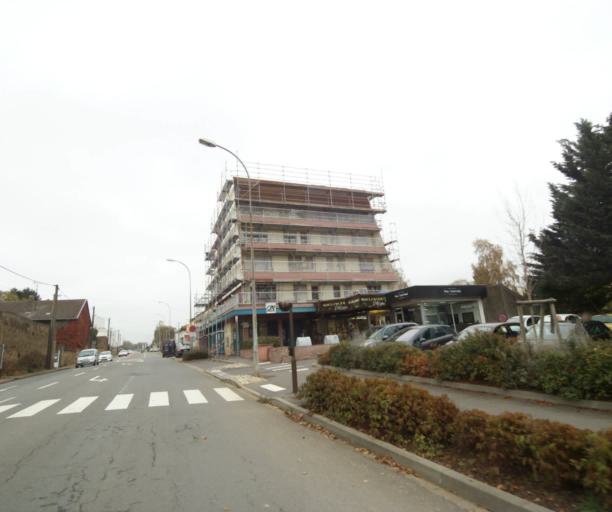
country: FR
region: Lorraine
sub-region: Departement de Meurthe-et-Moselle
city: Briey
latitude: 49.2499
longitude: 5.9431
